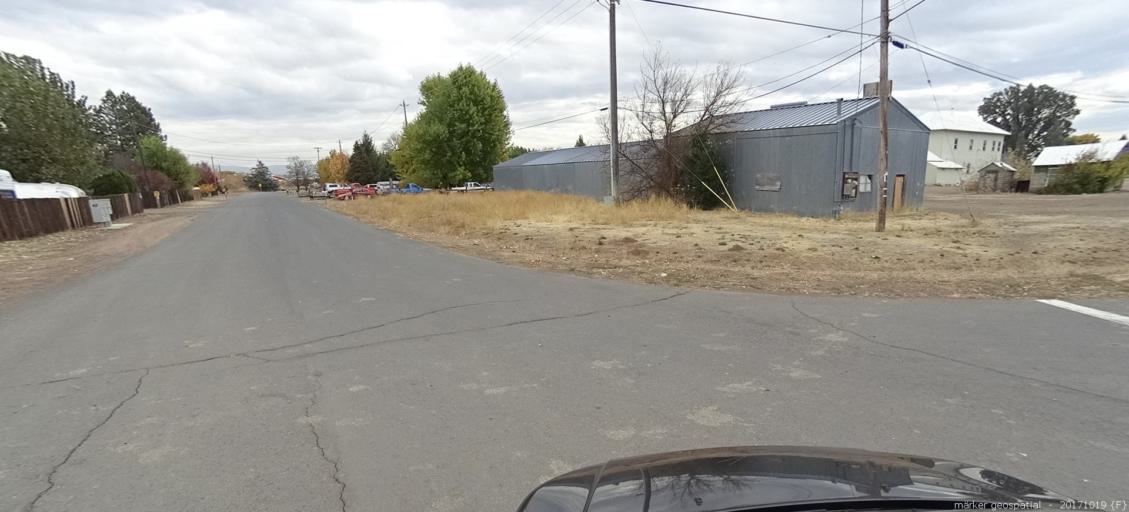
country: US
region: California
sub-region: Shasta County
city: Burney
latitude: 41.0514
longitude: -121.3984
